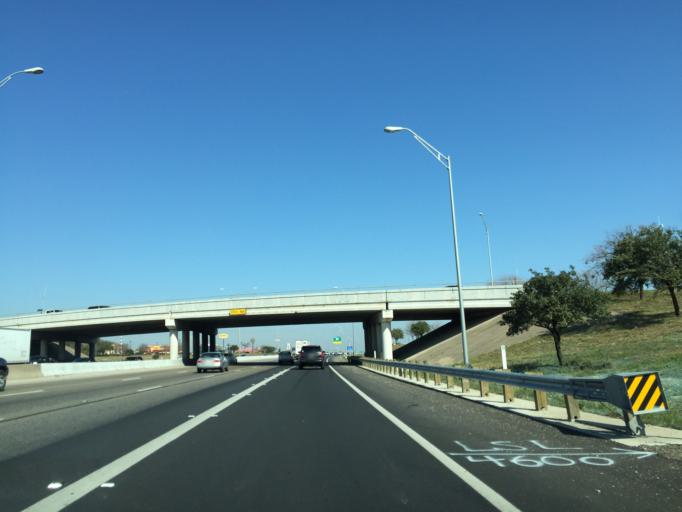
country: US
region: Texas
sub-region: Williamson County
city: Round Rock
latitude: 30.5345
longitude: -97.6918
